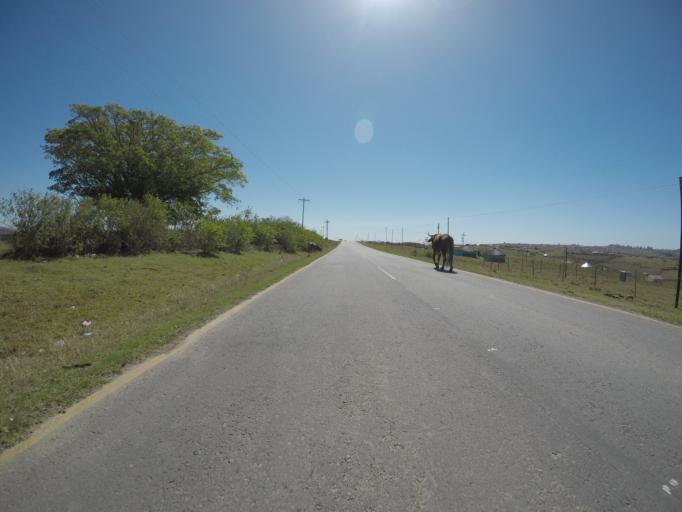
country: ZA
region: Eastern Cape
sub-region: OR Tambo District Municipality
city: Libode
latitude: -31.9110
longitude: 28.9956
